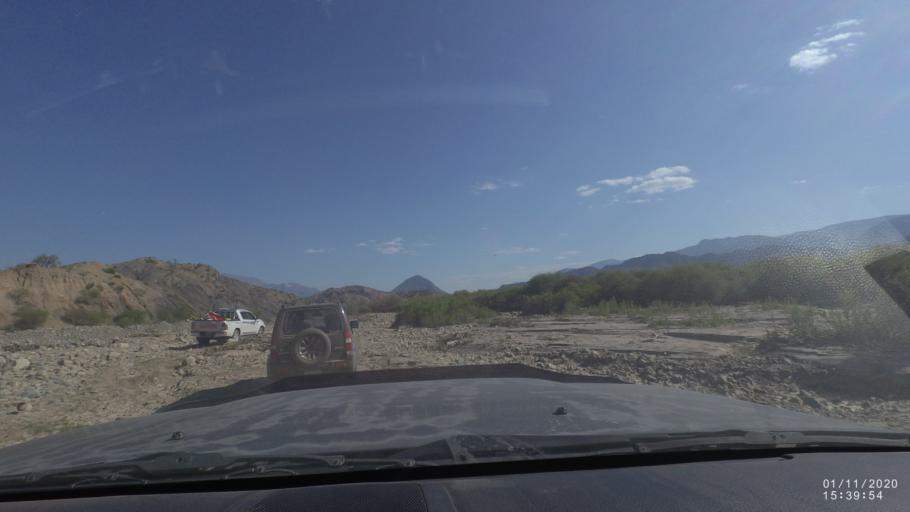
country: BO
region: Chuquisaca
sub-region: Provincia Zudanez
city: Mojocoya
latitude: -18.6775
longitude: -64.5024
